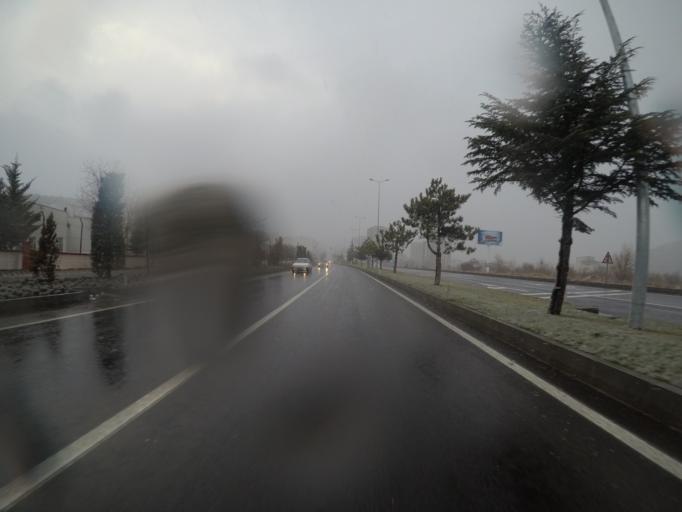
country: TR
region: Nevsehir
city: Nevsehir
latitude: 38.6319
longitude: 34.7480
